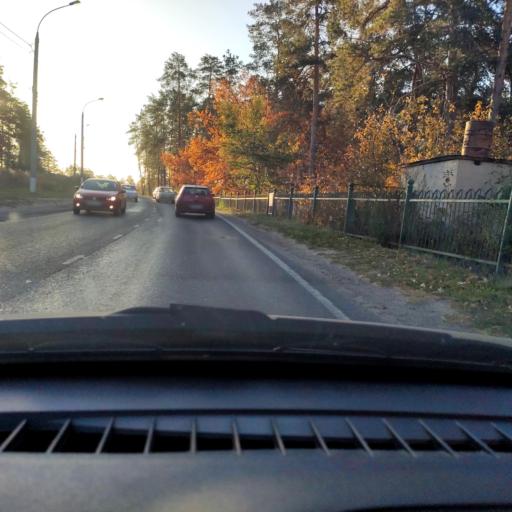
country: RU
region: Samara
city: Tol'yatti
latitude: 53.4833
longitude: 49.3179
